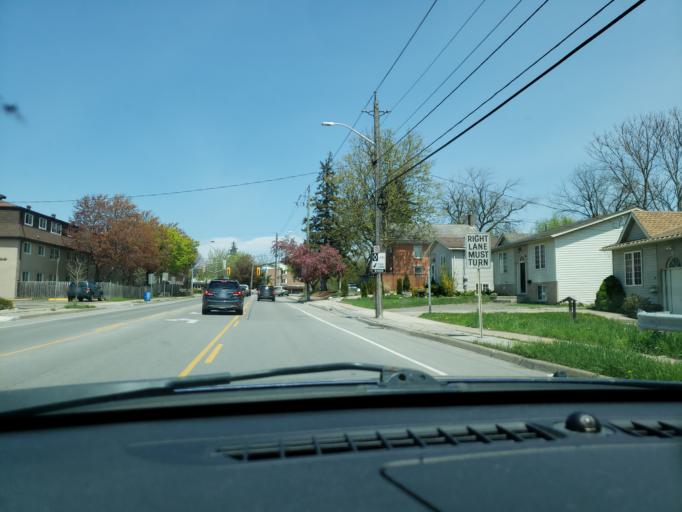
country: CA
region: Ontario
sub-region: Regional Municipality of Niagara
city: St. Catharines
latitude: 43.1576
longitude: -79.2144
